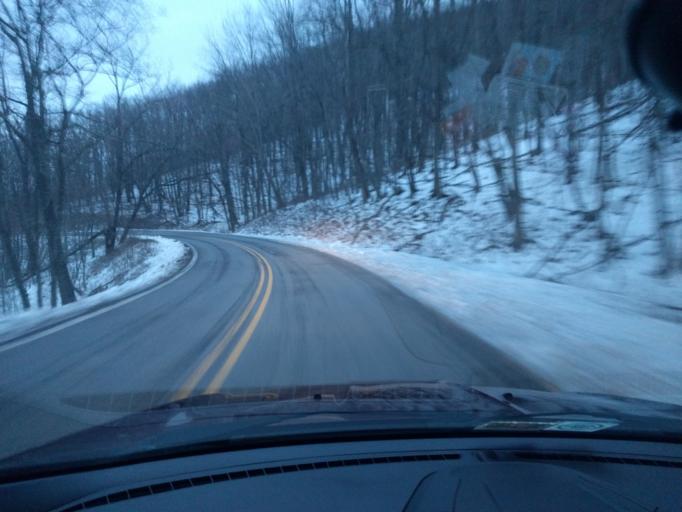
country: US
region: Virginia
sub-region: Alleghany County
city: Clifton Forge
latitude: 37.8814
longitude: -79.8884
